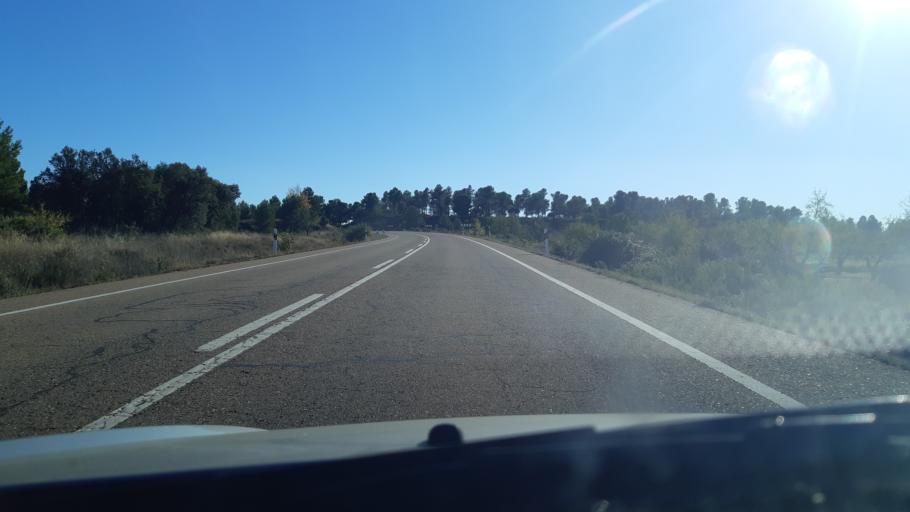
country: ES
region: Aragon
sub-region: Provincia de Teruel
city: Valjunquera
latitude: 40.9440
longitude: -0.0117
